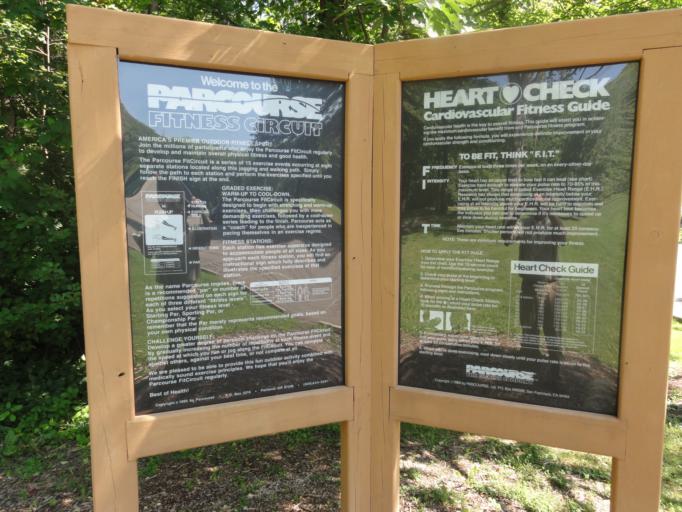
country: US
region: Ohio
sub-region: Cuyahoga County
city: Moreland Hills
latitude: 41.4176
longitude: -81.4198
